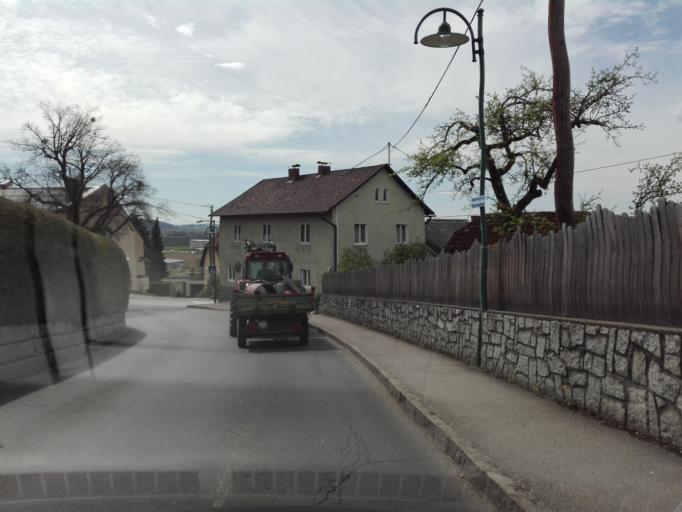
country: AT
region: Upper Austria
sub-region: Politischer Bezirk Urfahr-Umgebung
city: Walding
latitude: 48.3512
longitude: 14.1597
